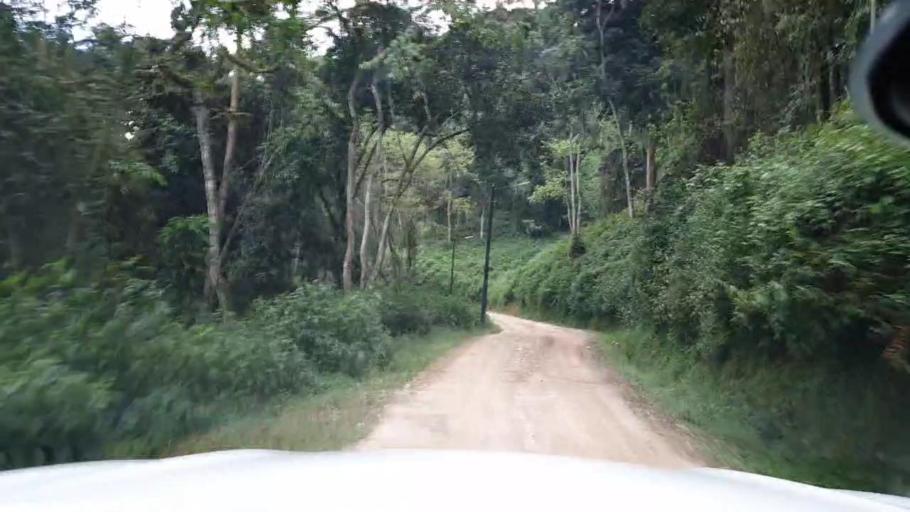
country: RW
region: Western Province
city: Cyangugu
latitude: -2.5636
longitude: 29.2280
